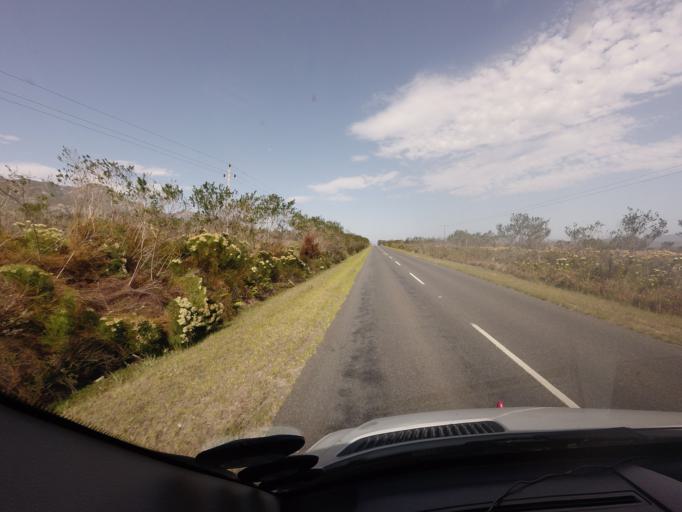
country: ZA
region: Western Cape
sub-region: Overberg District Municipality
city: Hermanus
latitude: -34.4121
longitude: 19.4043
